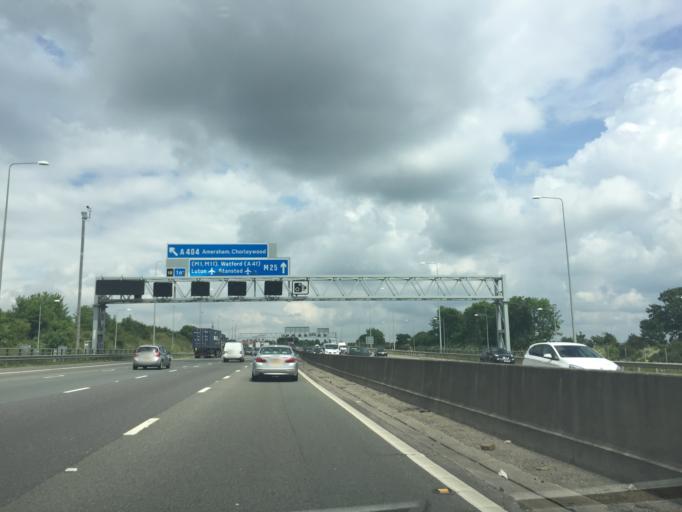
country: GB
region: England
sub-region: Hertfordshire
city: Chorleywood
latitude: 51.6383
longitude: -0.5095
